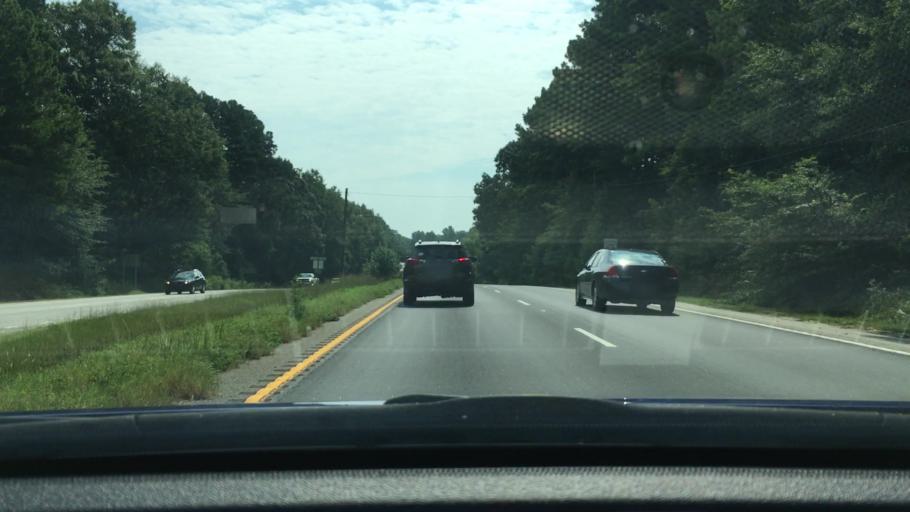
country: US
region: South Carolina
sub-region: Sumter County
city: Stateburg
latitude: 33.9453
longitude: -80.5222
